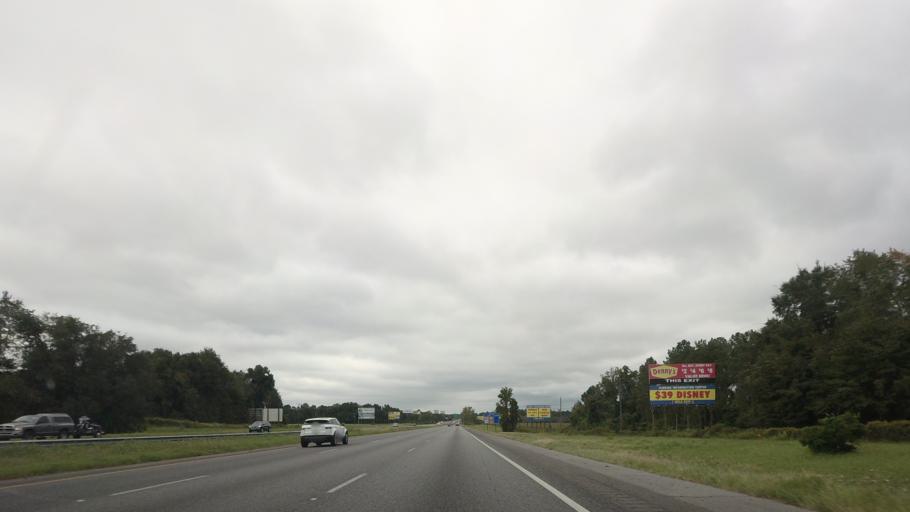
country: US
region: Georgia
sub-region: Echols County
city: Statenville
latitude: 30.6594
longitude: -83.2049
